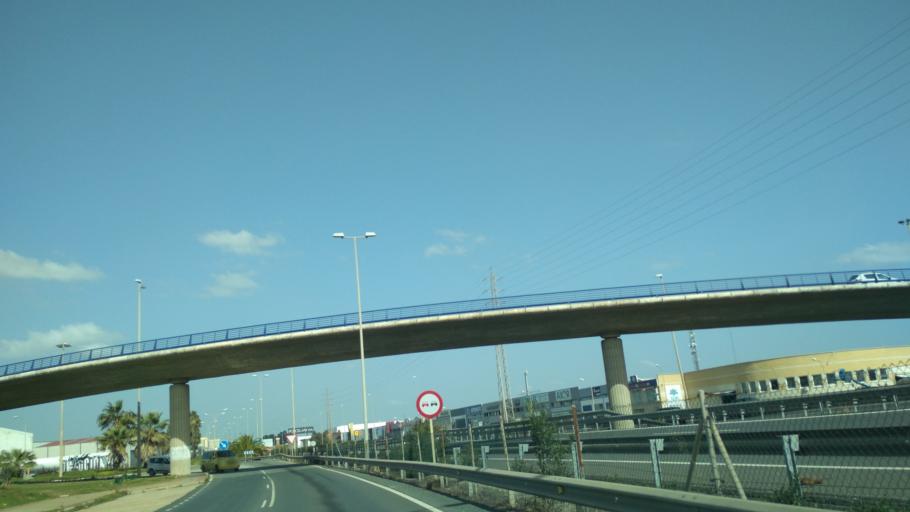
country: ES
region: Andalusia
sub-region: Provincia de Huelva
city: Huelva
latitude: 37.2597
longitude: -6.9208
